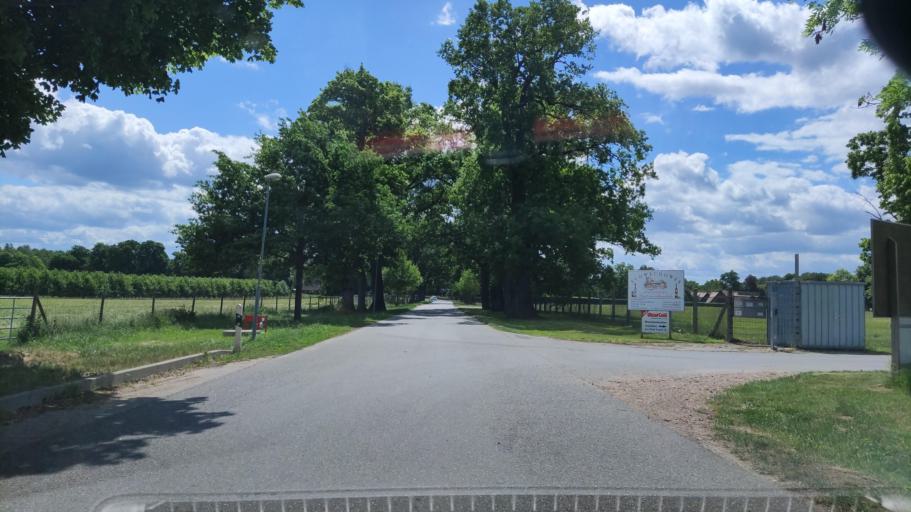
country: DE
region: Mecklenburg-Vorpommern
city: Lubtheen
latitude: 53.3856
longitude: 11.0553
